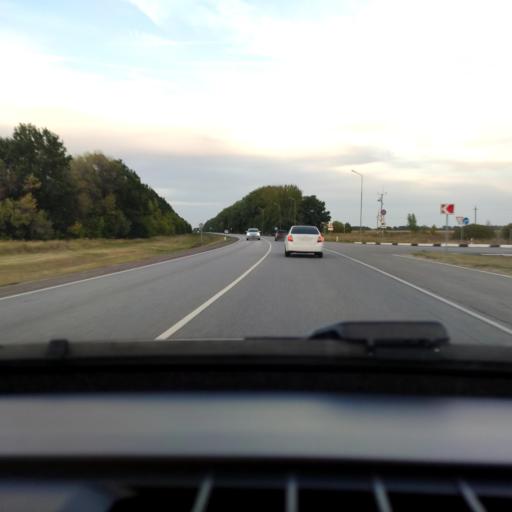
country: RU
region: Voronezj
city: Kashirskoye
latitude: 51.4706
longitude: 39.9002
